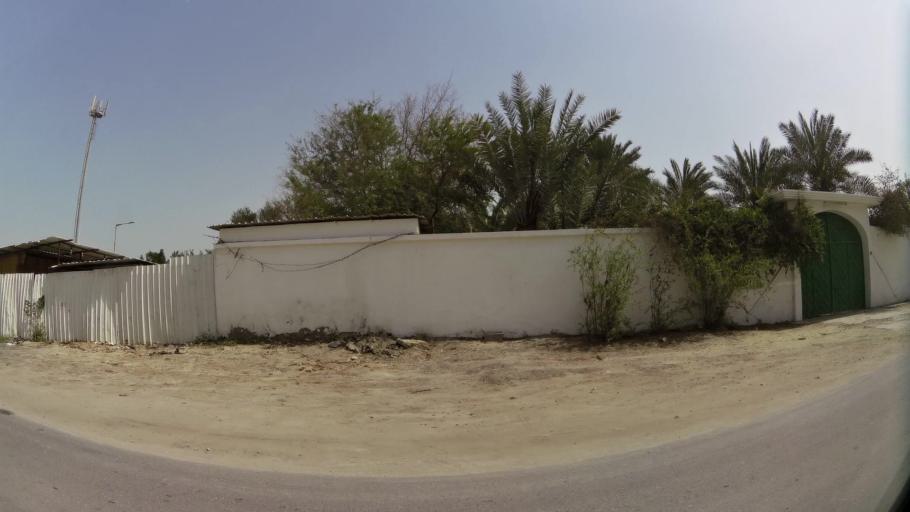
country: BH
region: Manama
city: Jidd Hafs
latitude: 26.2263
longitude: 50.4822
